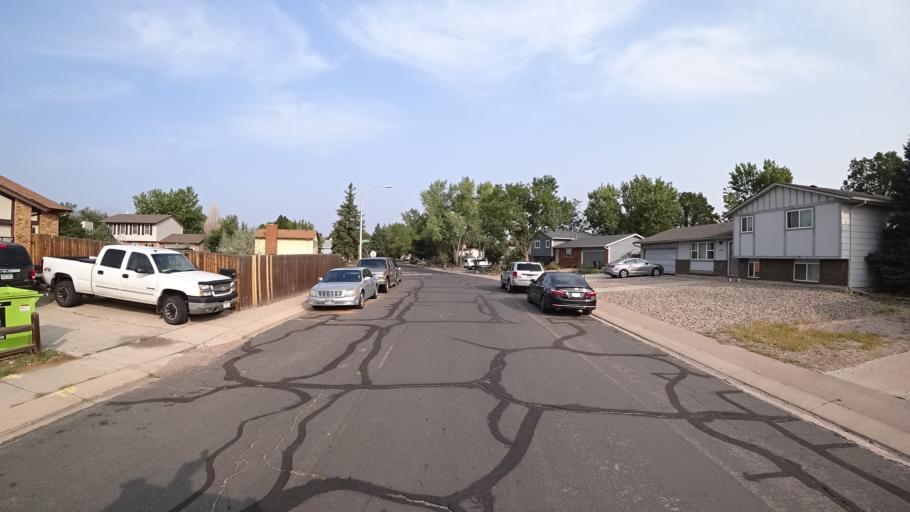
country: US
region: Colorado
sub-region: El Paso County
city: Stratmoor
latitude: 38.8001
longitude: -104.7389
